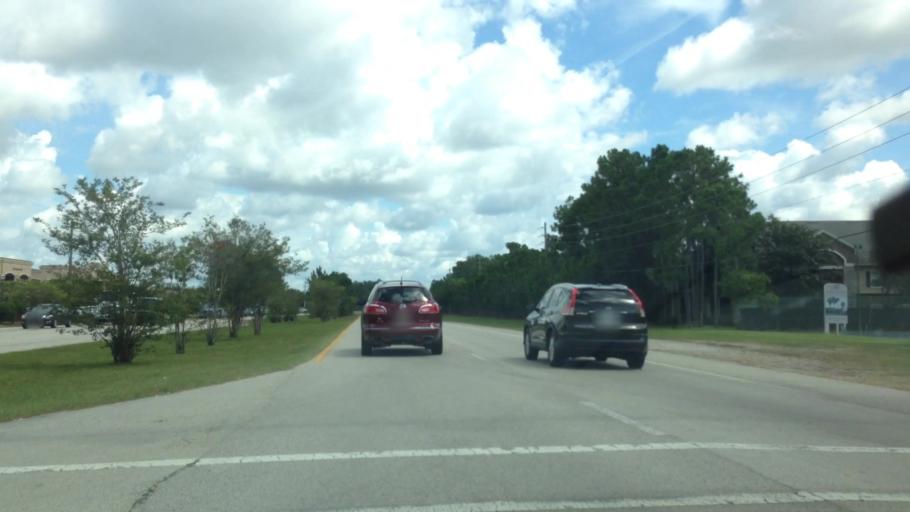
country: US
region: Florida
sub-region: Duval County
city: Jacksonville Beach
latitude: 30.2573
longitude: -81.4665
